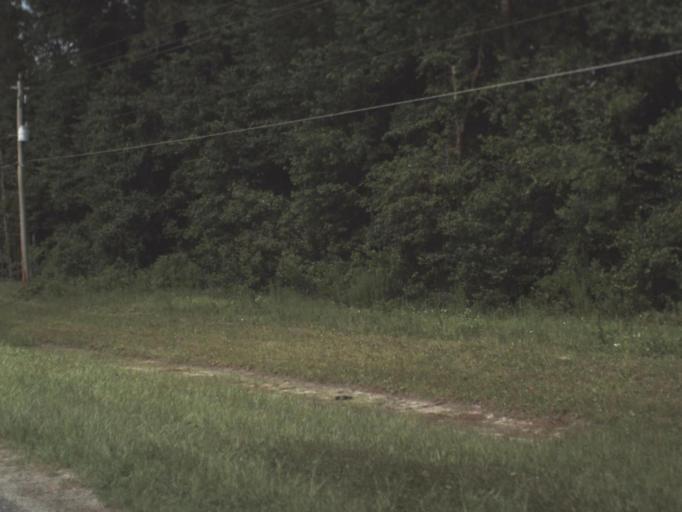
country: US
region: Florida
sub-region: Columbia County
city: Five Points
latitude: 30.2542
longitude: -82.6381
